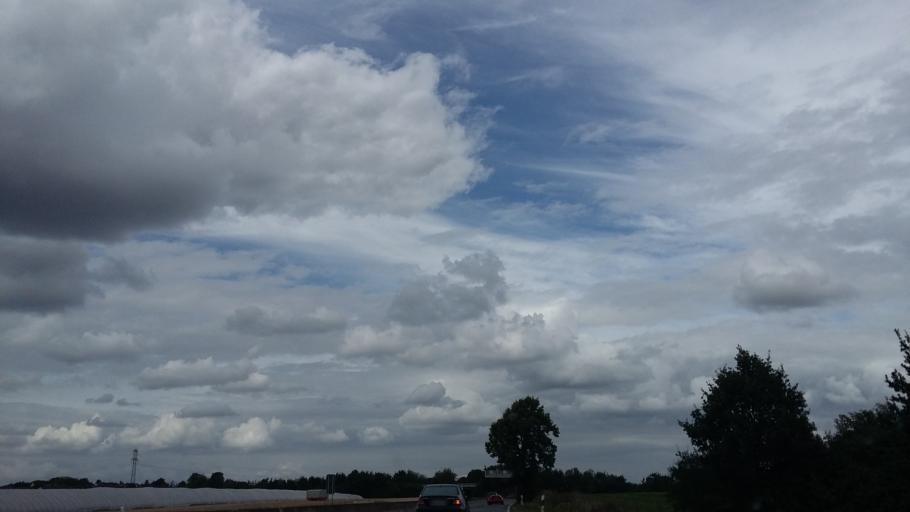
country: DE
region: Lower Saxony
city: Sarstedt
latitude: 52.2757
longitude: 9.8469
